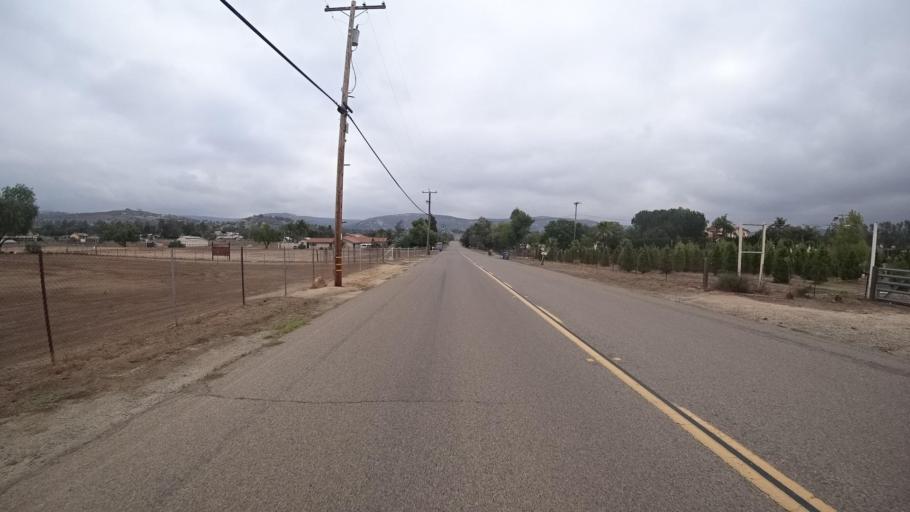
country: US
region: California
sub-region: San Diego County
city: Ramona
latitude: 33.0658
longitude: -116.8659
